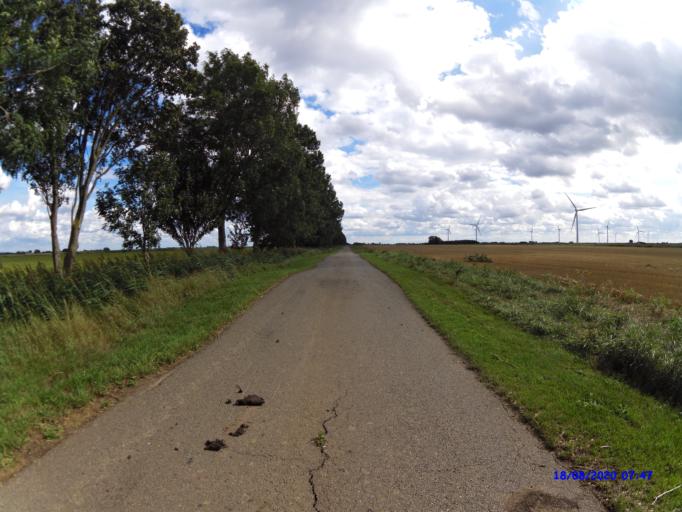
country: GB
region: England
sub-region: Cambridgeshire
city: Whittlesey
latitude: 52.5232
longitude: -0.0985
